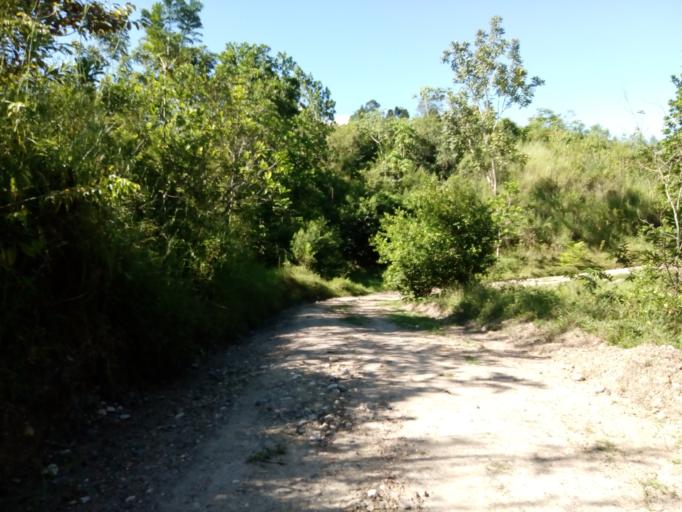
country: CO
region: Boyaca
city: Puerto Boyaca
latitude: 6.0039
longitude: -74.3708
